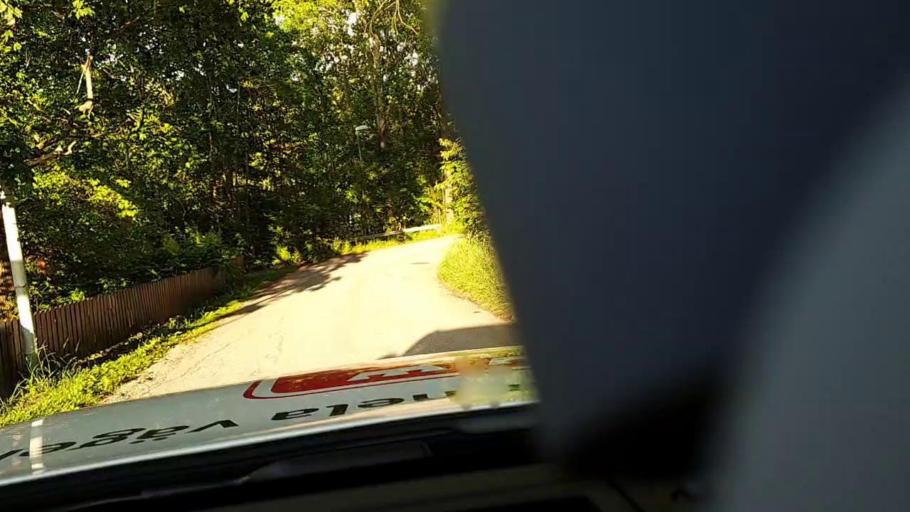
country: SE
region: Stockholm
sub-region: Huddinge Kommun
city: Huddinge
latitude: 59.2446
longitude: 17.9741
